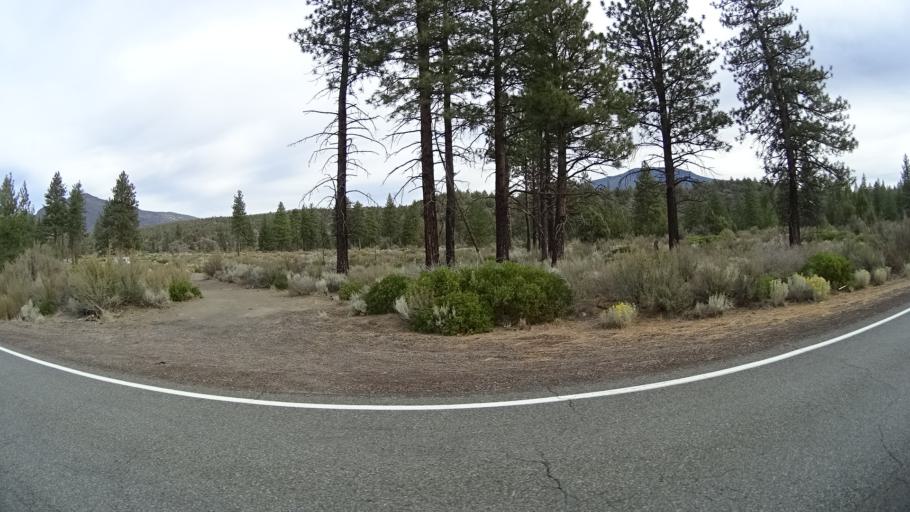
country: US
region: California
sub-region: Siskiyou County
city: Weed
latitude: 41.5414
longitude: -122.2456
